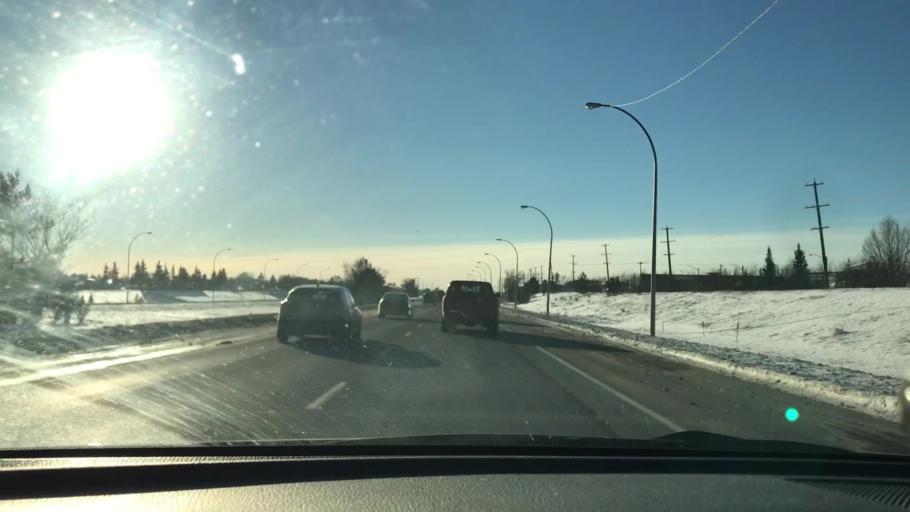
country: CA
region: Alberta
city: Edmonton
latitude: 53.4788
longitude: -113.4669
